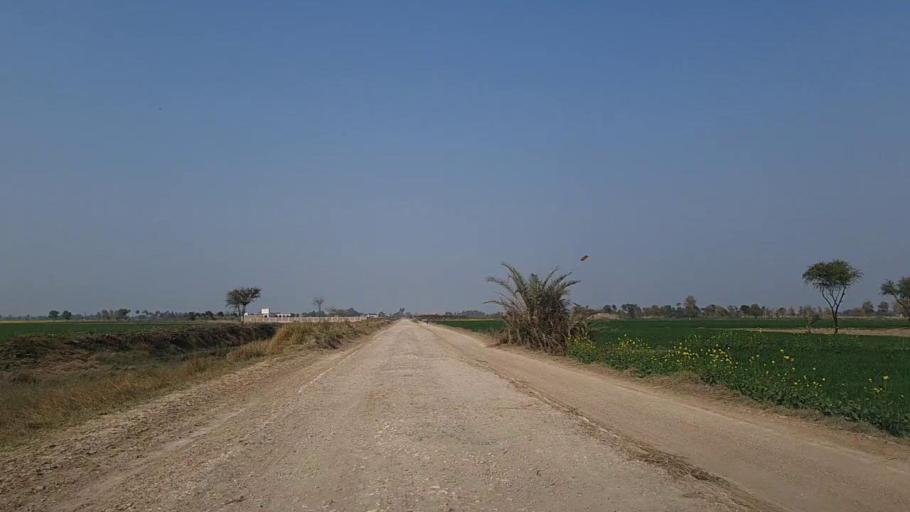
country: PK
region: Sindh
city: Daur
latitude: 26.4168
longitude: 68.4088
